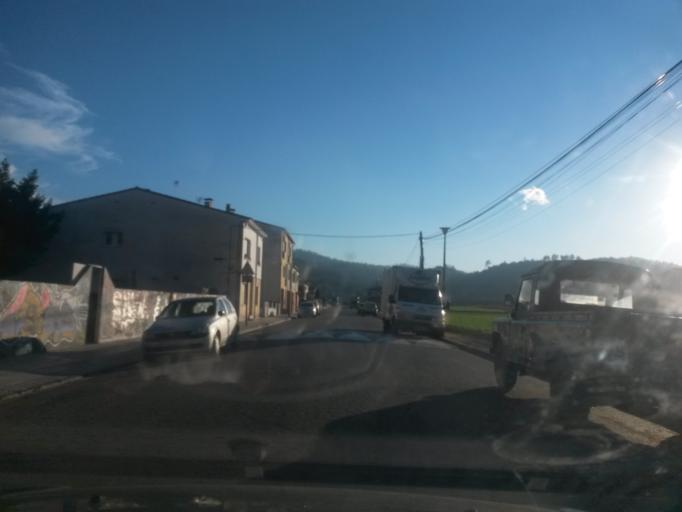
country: ES
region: Catalonia
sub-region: Provincia de Girona
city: Bescano
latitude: 41.9657
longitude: 2.7354
